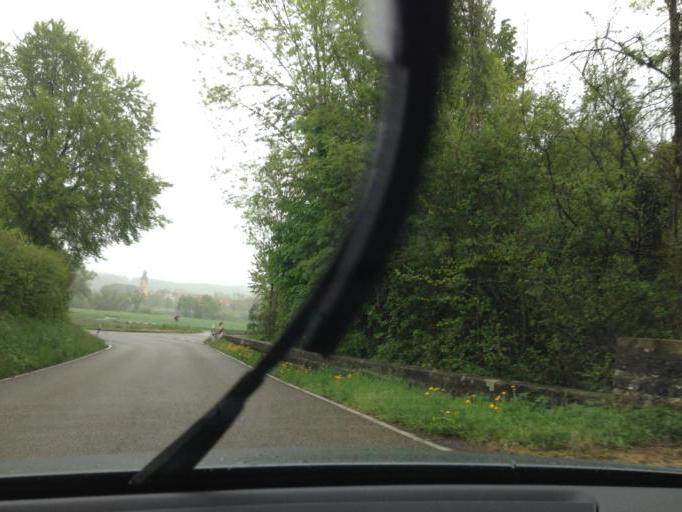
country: DE
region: Baden-Wuerttemberg
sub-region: Regierungsbezirk Stuttgart
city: Offenau
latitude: 49.2429
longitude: 9.1546
